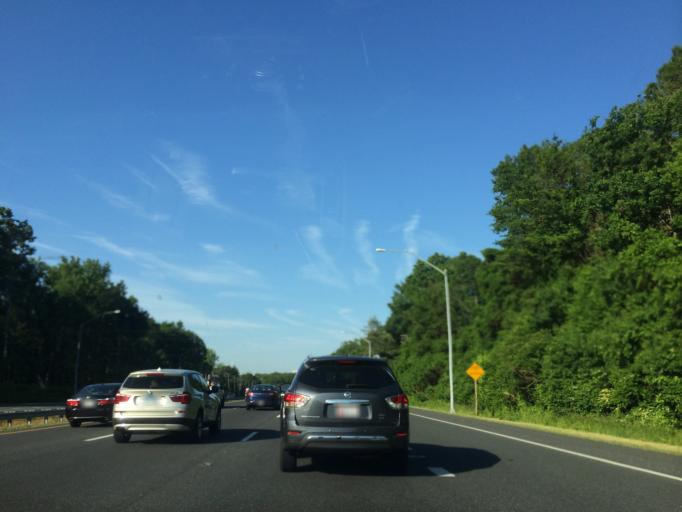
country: US
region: Maryland
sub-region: Howard County
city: Riverside
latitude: 39.1760
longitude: -76.8792
